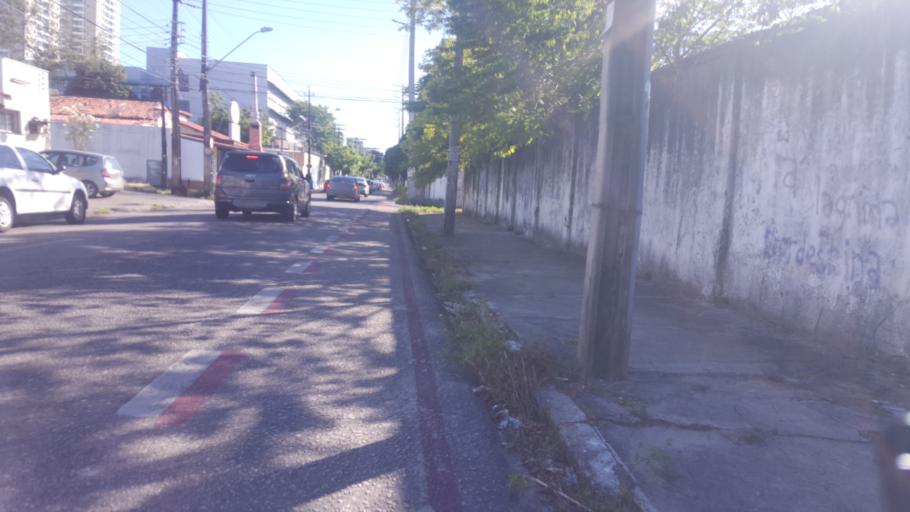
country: BR
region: Ceara
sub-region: Fortaleza
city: Fortaleza
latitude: -3.7443
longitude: -38.5338
